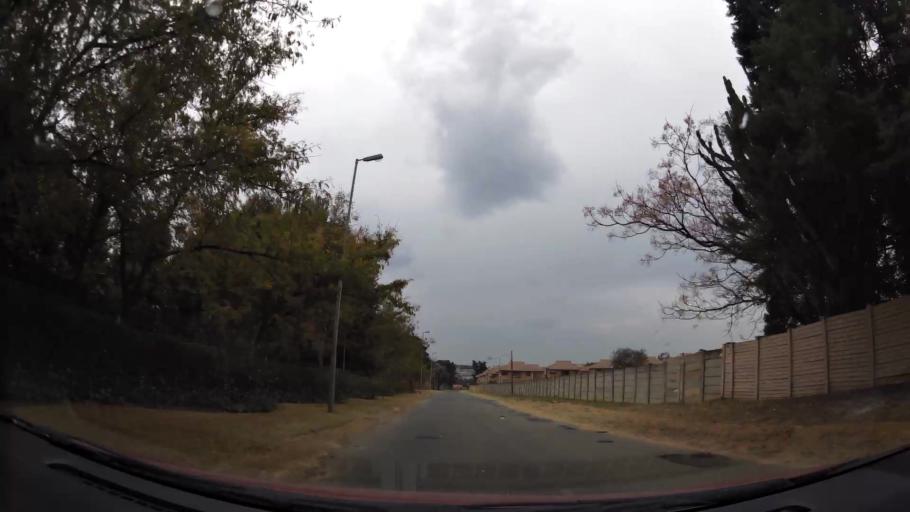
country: ZA
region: Gauteng
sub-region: City of Johannesburg Metropolitan Municipality
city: Roodepoort
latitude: -26.0952
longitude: 27.9136
